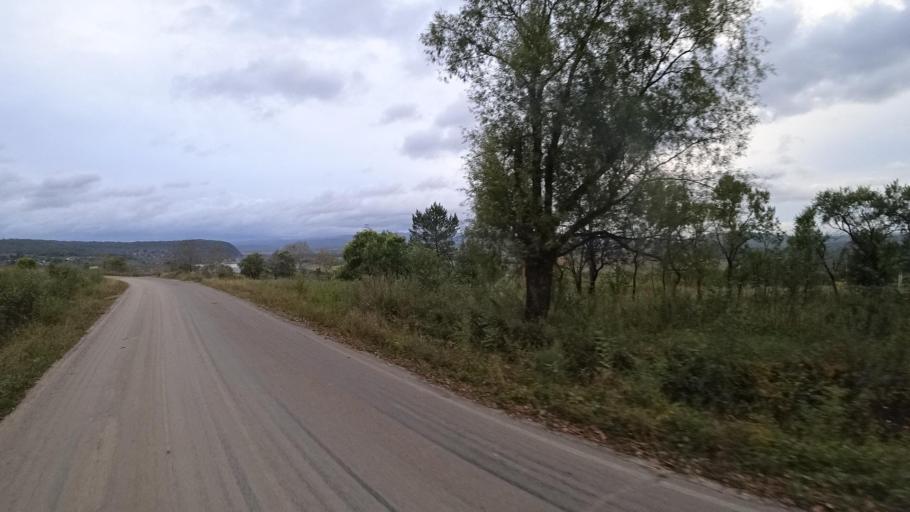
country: RU
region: Jewish Autonomous Oblast
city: Izvestkovyy
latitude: 48.9764
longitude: 131.5698
